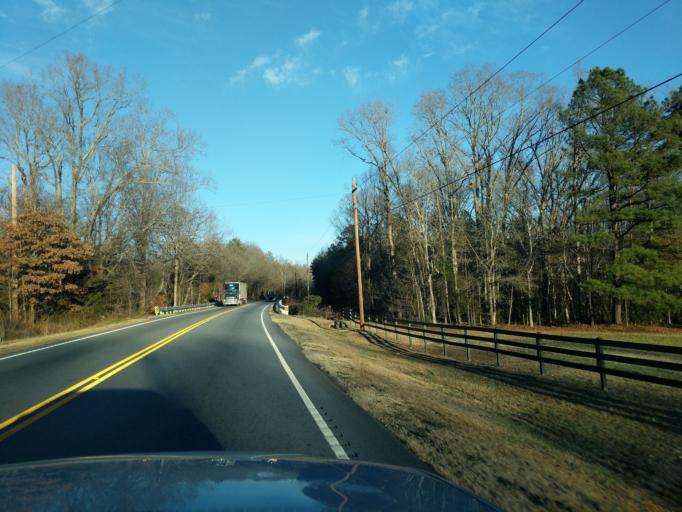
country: US
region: South Carolina
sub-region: Greenville County
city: Simpsonville
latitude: 34.6581
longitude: -82.2791
